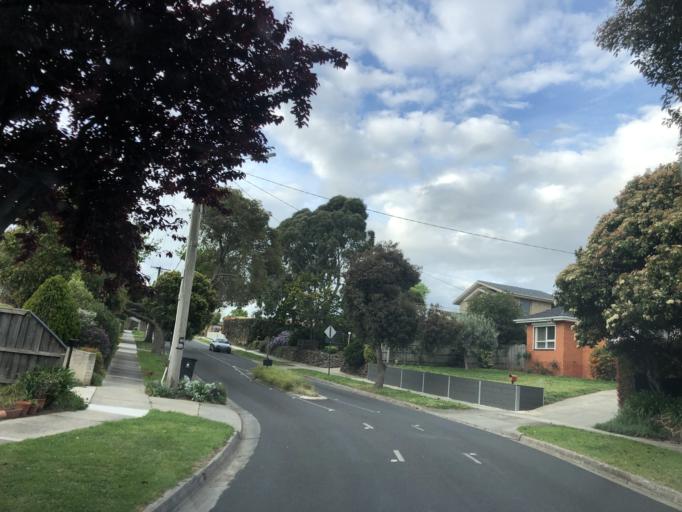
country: AU
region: Victoria
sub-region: Whitehorse
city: Burwood
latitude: -37.8616
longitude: 145.1197
